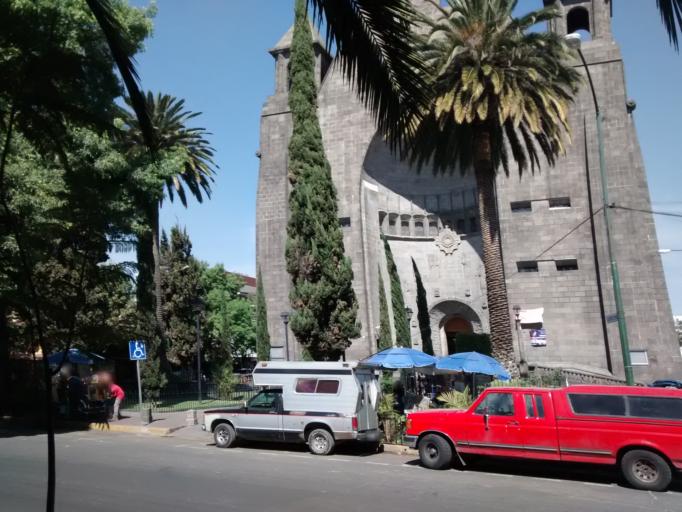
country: MX
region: Mexico City
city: Miguel Hidalgo
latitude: 19.4344
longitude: -99.1964
